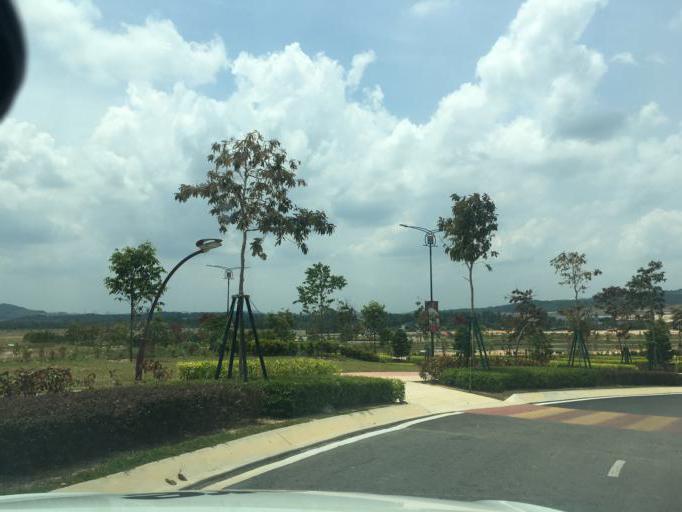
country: MY
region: Putrajaya
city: Putrajaya
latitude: 2.8440
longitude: 101.6958
